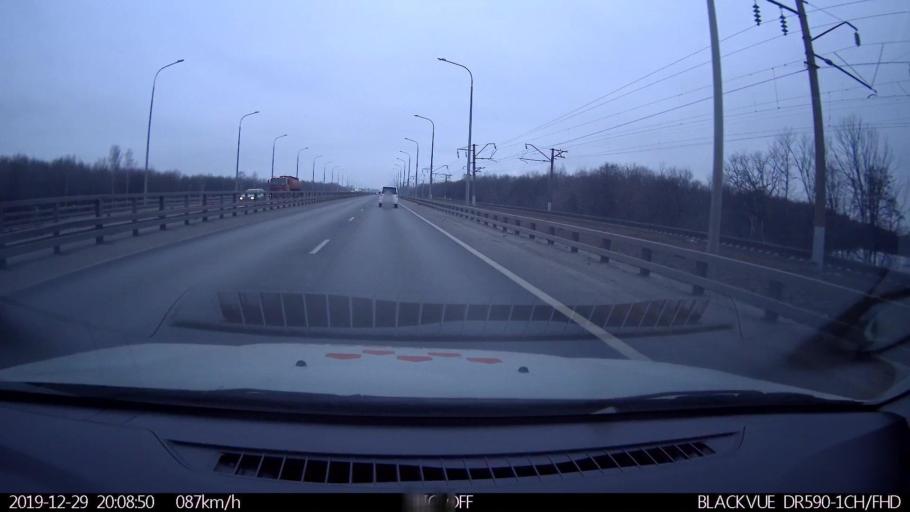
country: RU
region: Nizjnij Novgorod
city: Neklyudovo
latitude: 56.3809
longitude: 43.9594
